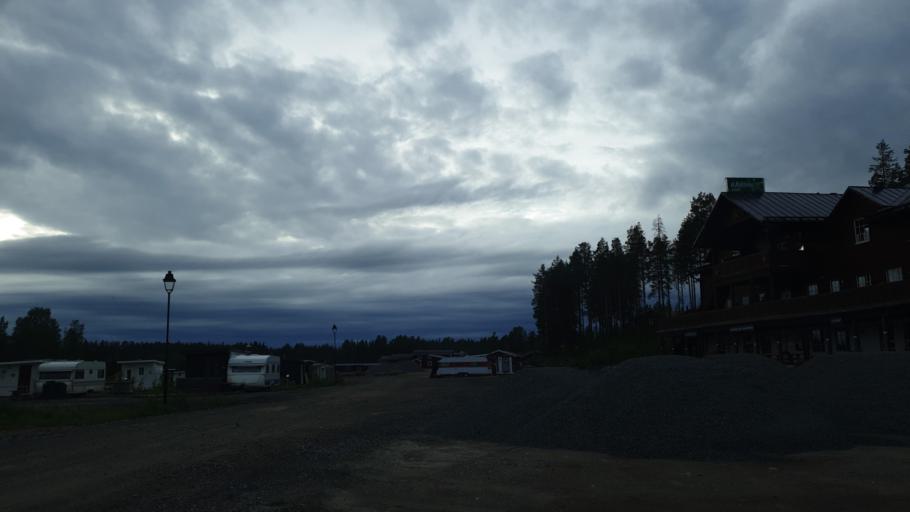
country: SE
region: Norrbotten
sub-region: Jokkmokks Kommun
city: Jokkmokk
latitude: 66.1548
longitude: 19.9898
